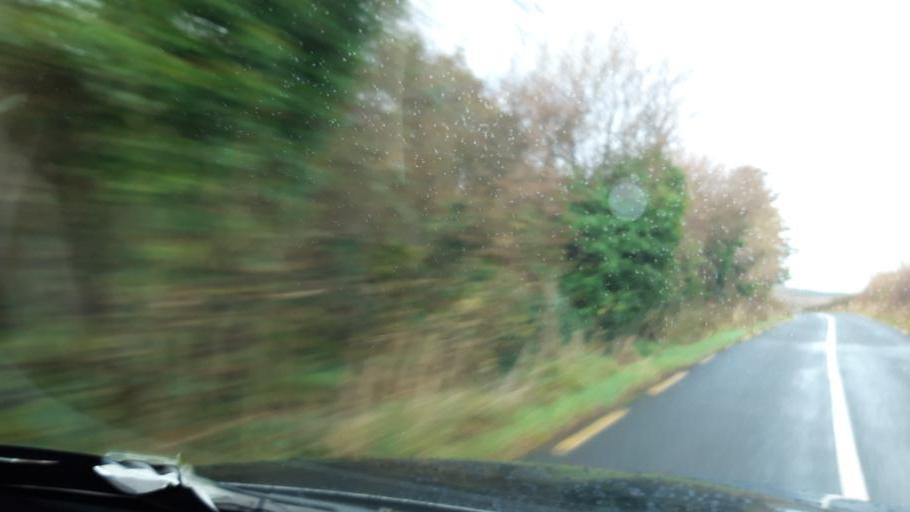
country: IE
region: Ulster
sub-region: County Donegal
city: Buncrana
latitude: 55.1597
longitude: -7.5655
